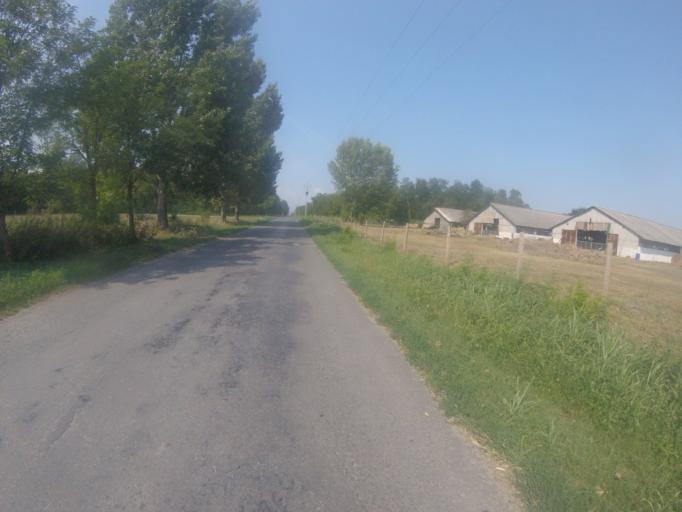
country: HU
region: Bacs-Kiskun
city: Ersekcsanad
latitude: 46.2541
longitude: 18.9639
